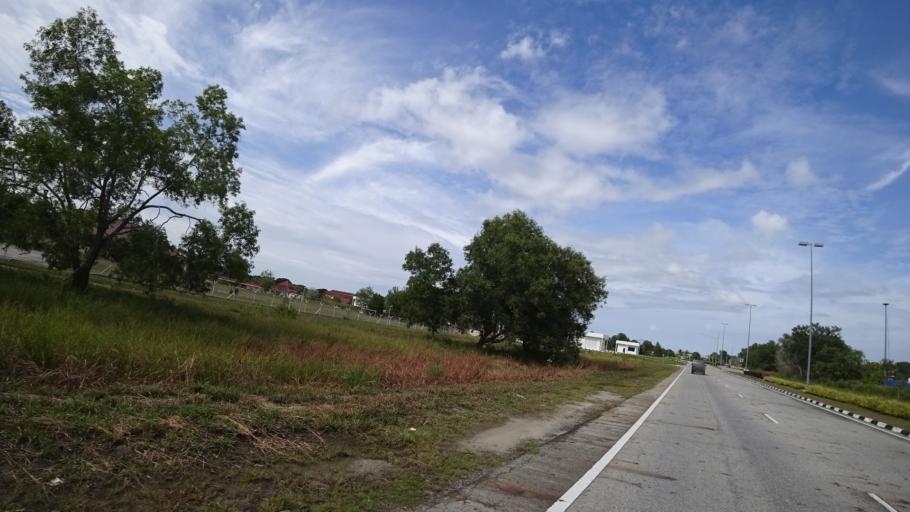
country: BN
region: Tutong
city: Tutong
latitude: 4.8138
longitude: 114.6568
